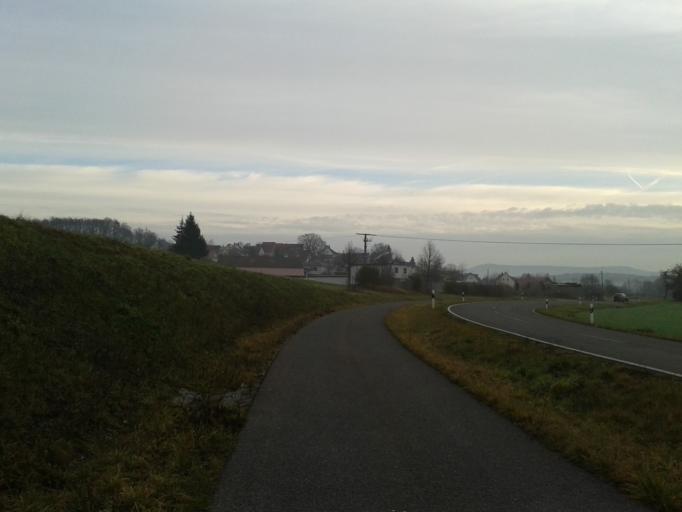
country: DE
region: Bavaria
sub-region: Upper Franconia
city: Memmelsdorf
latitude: 49.9403
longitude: 10.9435
